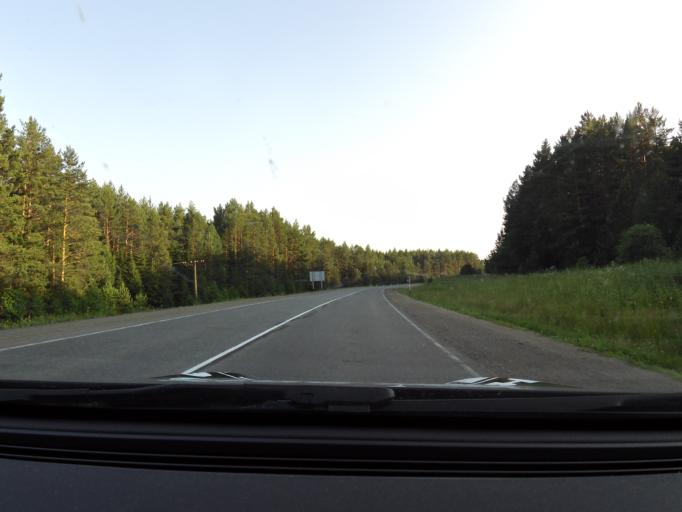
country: RU
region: Sverdlovsk
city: Nizhniye Sergi
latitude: 56.6377
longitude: 59.2479
